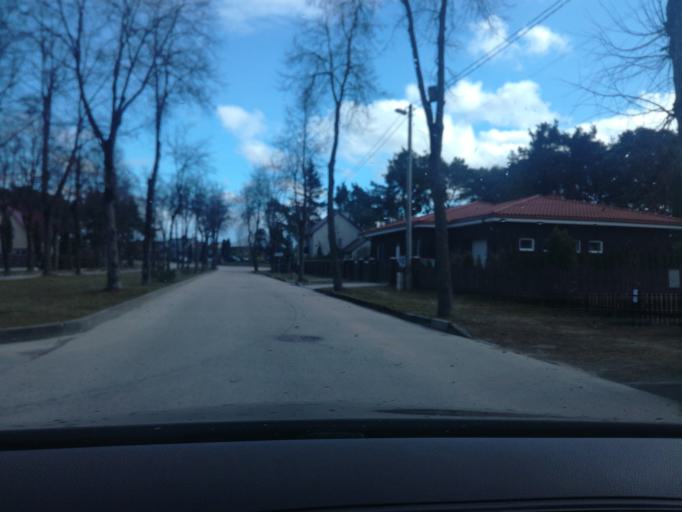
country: LT
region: Alytaus apskritis
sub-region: Alytus
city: Alytus
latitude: 54.3899
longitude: 24.0498
